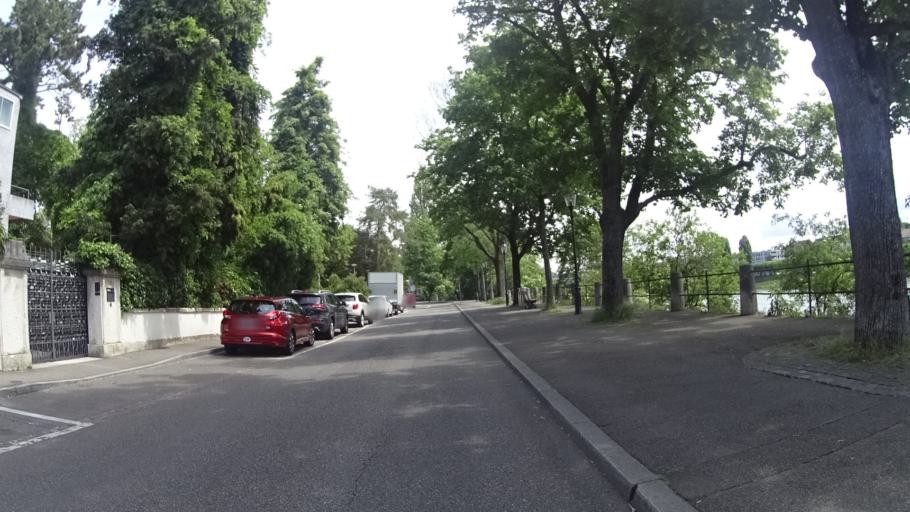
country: CH
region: Basel-Landschaft
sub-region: Bezirk Arlesheim
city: Birsfelden
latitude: 47.5573
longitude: 7.6041
